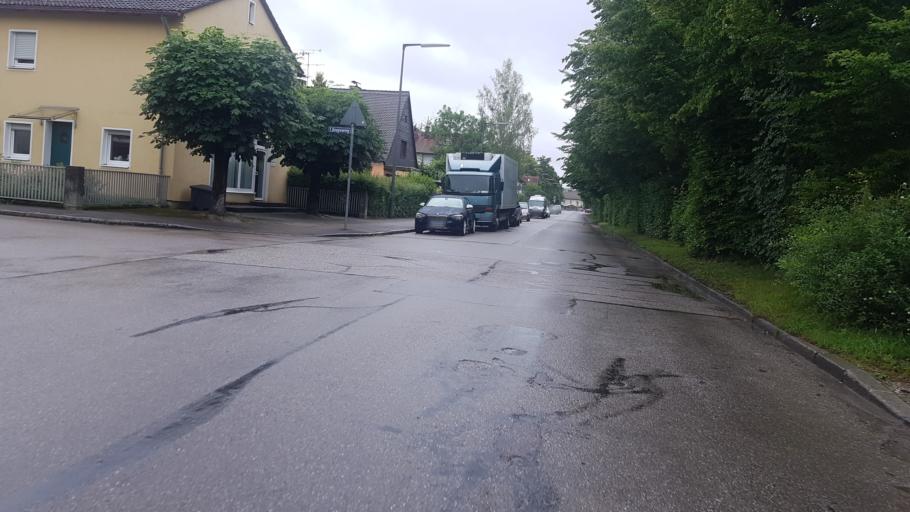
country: DE
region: Bavaria
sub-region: Upper Bavaria
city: Unterfoehring
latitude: 48.2042
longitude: 11.5939
